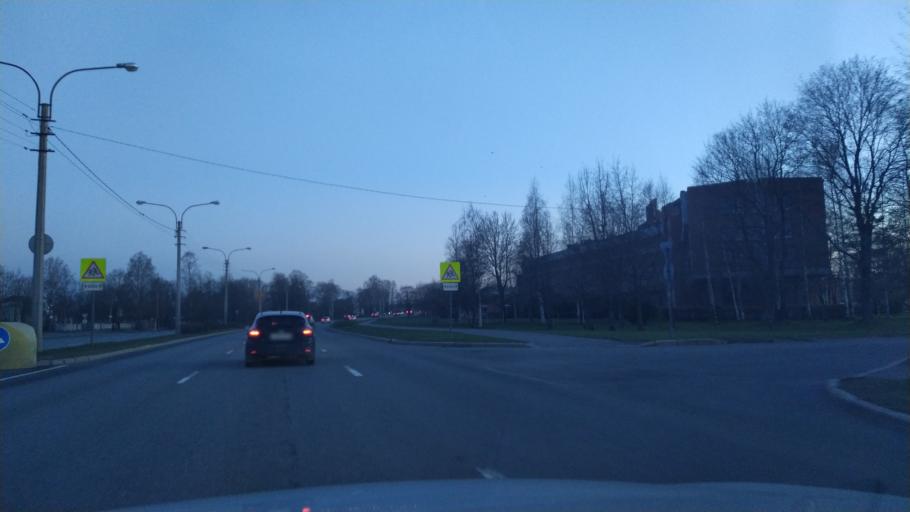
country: RU
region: St.-Petersburg
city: Sestroretsk
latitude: 60.0919
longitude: 29.9751
